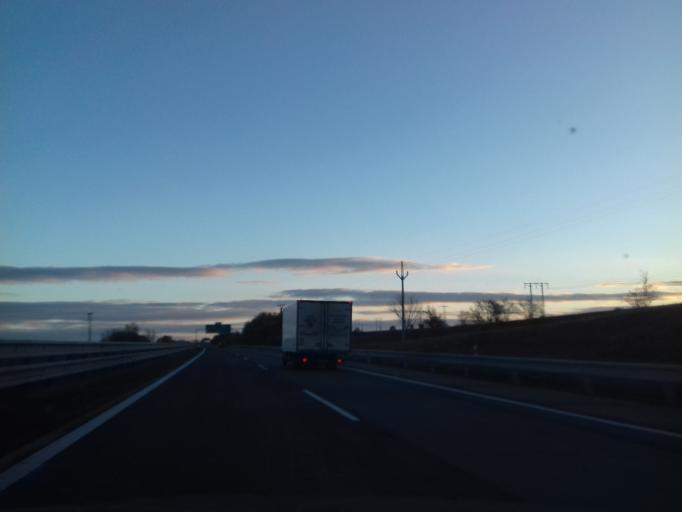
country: CZ
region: South Moravian
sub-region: Okres Vyskov
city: Vyskov
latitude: 49.2615
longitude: 16.9966
